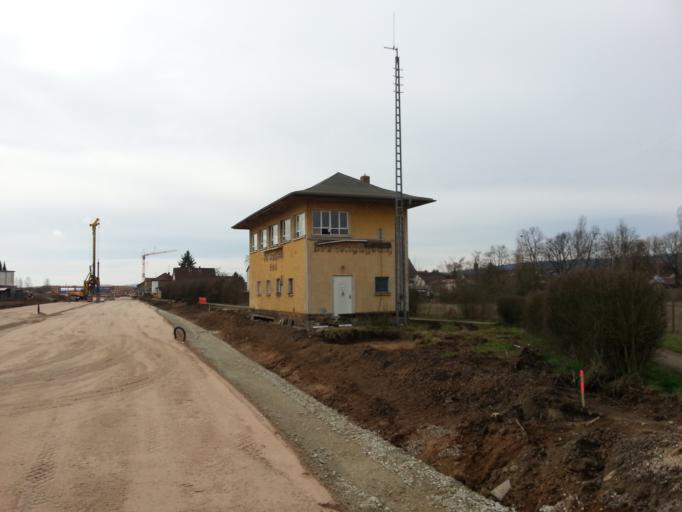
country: DE
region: Bavaria
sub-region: Upper Franconia
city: Breitengussbach
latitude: 49.9695
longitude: 10.8878
